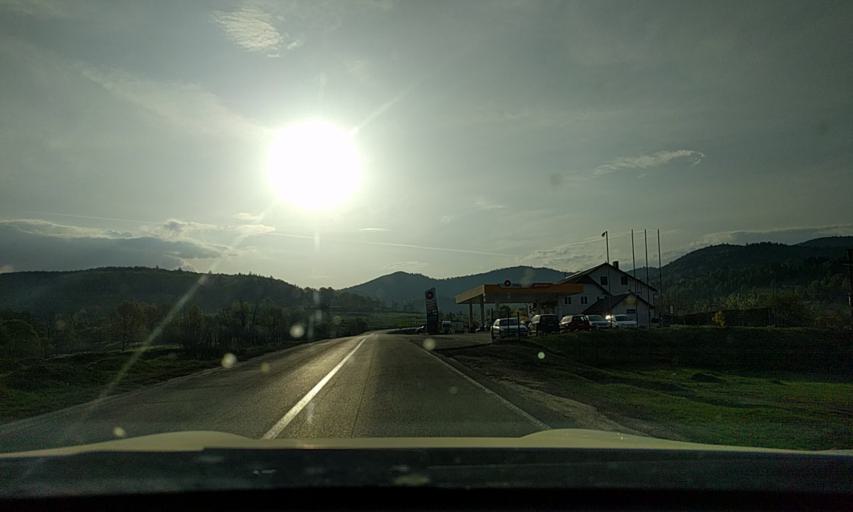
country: RO
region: Covasna
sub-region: Comuna Bretcu
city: Bretcu
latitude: 46.0452
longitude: 26.3252
